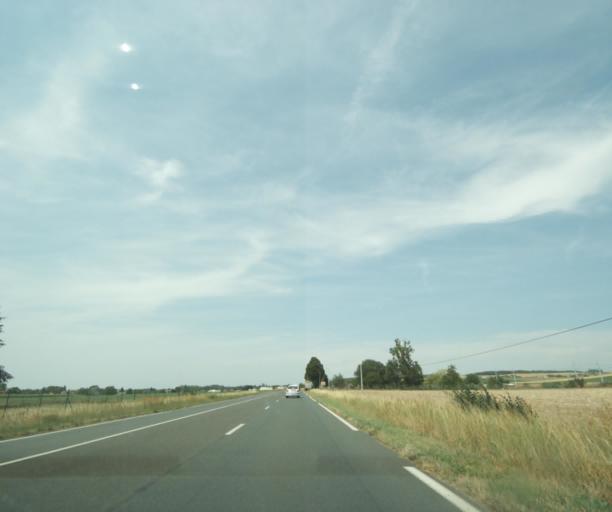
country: FR
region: Poitou-Charentes
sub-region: Departement de la Vienne
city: Dange-Saint-Romain
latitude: 46.9511
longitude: 0.6075
